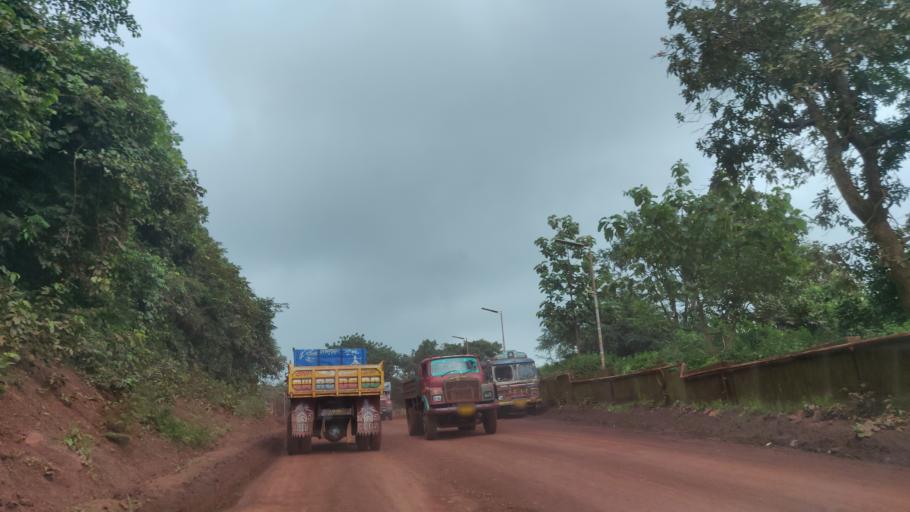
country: IN
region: Odisha
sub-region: Kendujhar
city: Barbil
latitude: 21.6299
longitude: 85.5125
